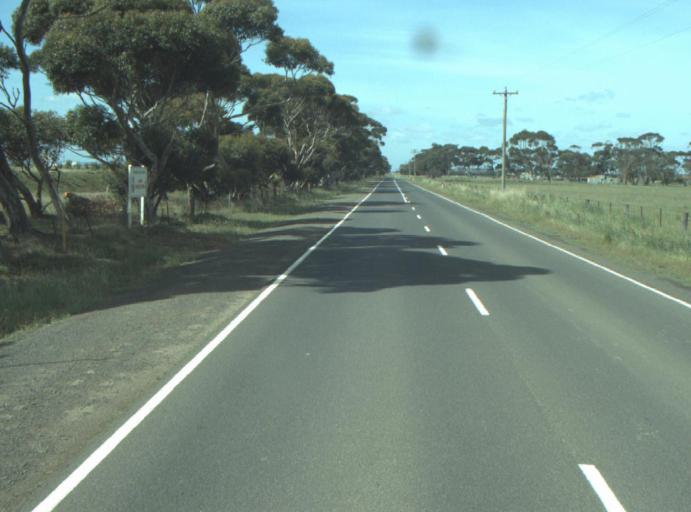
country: AU
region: Victoria
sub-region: Greater Geelong
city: Lara
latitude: -38.0515
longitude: 144.4284
